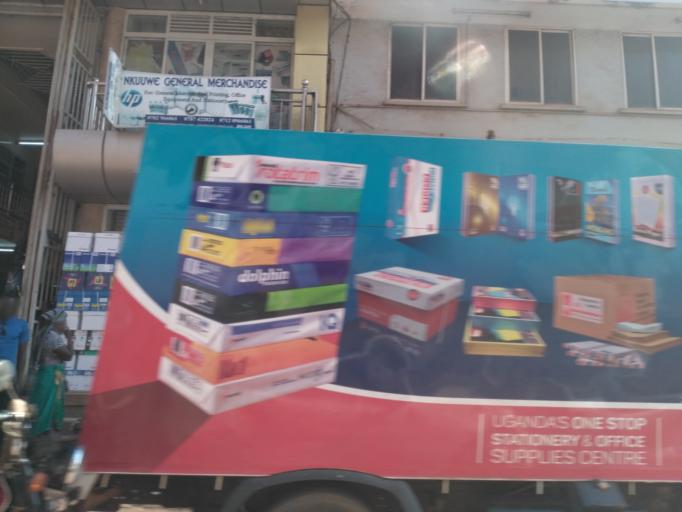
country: UG
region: Central Region
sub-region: Kampala District
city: Kampala
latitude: 0.3113
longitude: 32.5851
